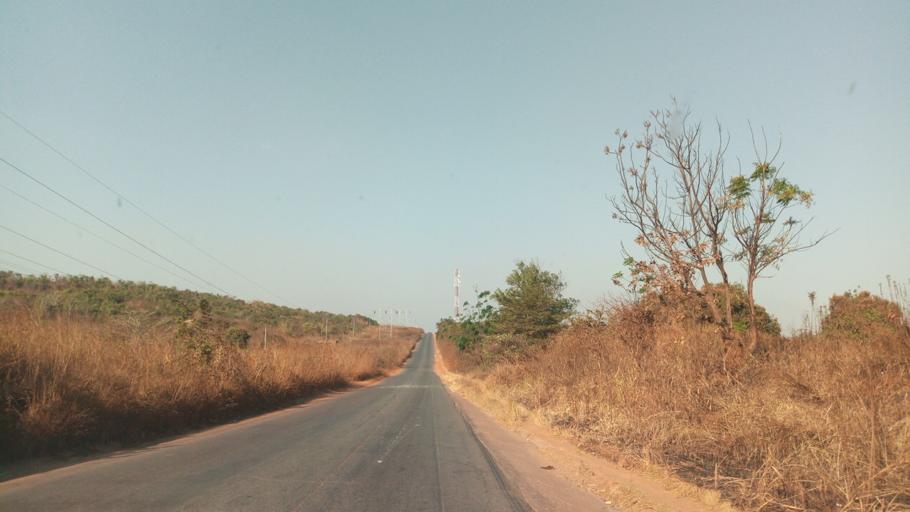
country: CD
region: Katanga
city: Likasi
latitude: -11.0003
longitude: 26.8854
